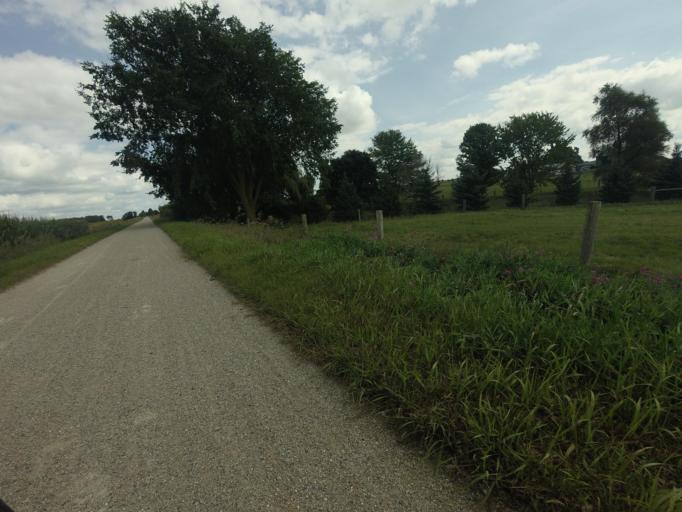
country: CA
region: Ontario
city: North Perth
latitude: 43.5772
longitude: -80.7984
